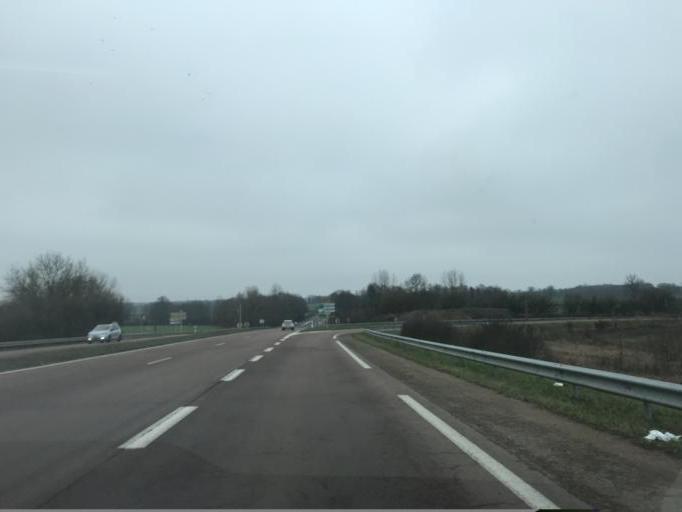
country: FR
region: Bourgogne
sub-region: Departement de l'Yonne
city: Avallon
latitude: 47.5037
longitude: 3.9922
